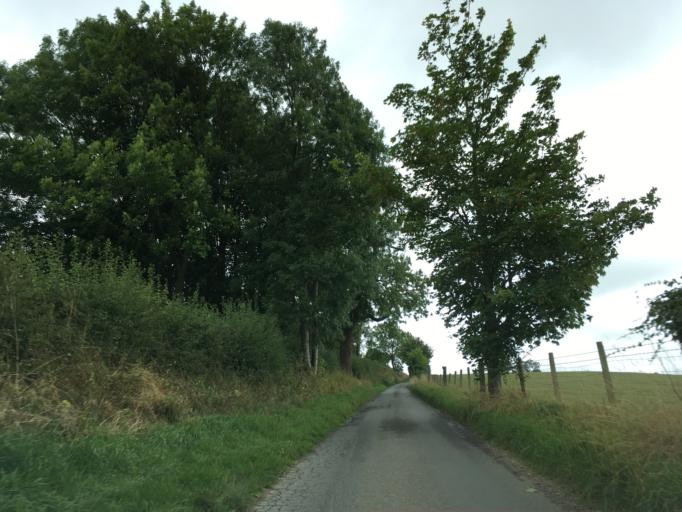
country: GB
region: England
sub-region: South Gloucestershire
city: Hinton
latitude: 51.5125
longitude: -2.3624
